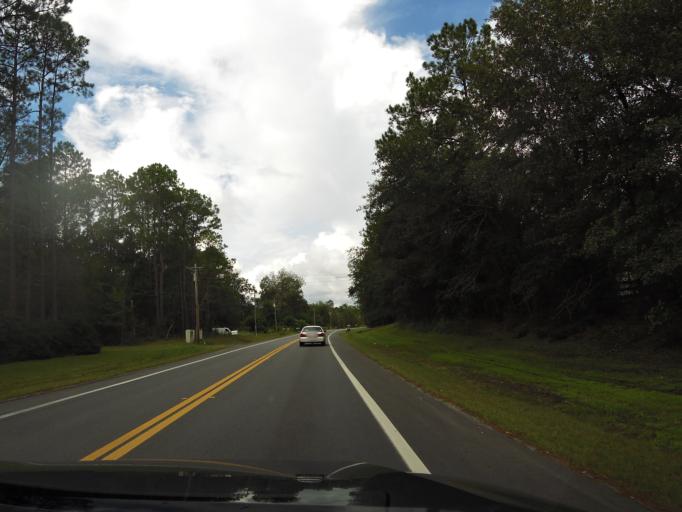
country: US
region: Florida
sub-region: Clay County
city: Middleburg
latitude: 30.1172
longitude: -81.9952
